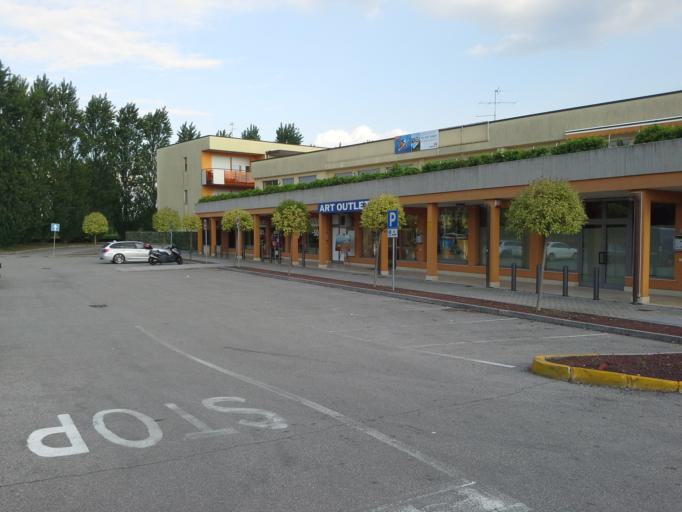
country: IT
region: Lombardy
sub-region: Provincia di Brescia
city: San Martino della Battaglia
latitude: 45.4604
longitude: 10.6266
